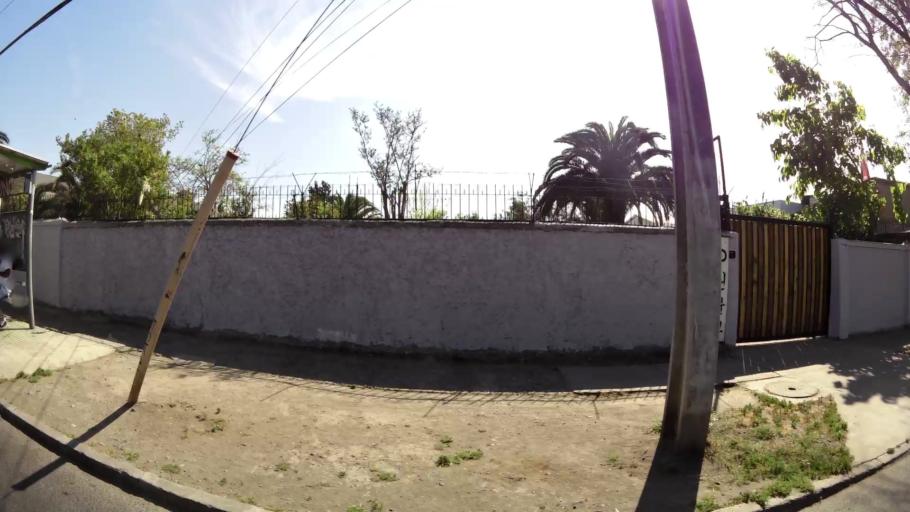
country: CL
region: Santiago Metropolitan
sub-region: Provincia de Santiago
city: Santiago
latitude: -33.3980
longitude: -70.6531
